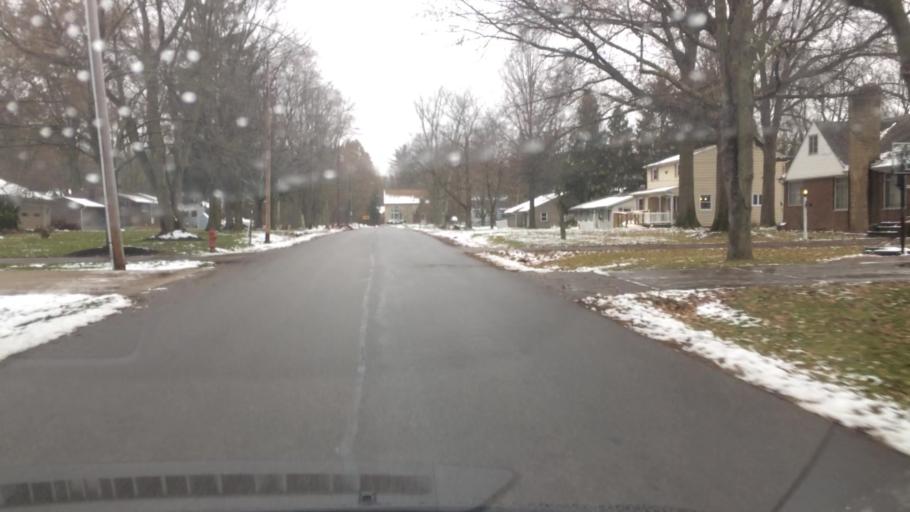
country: US
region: Ohio
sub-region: Cuyahoga County
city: Olmsted Falls
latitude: 41.3706
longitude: -81.9075
